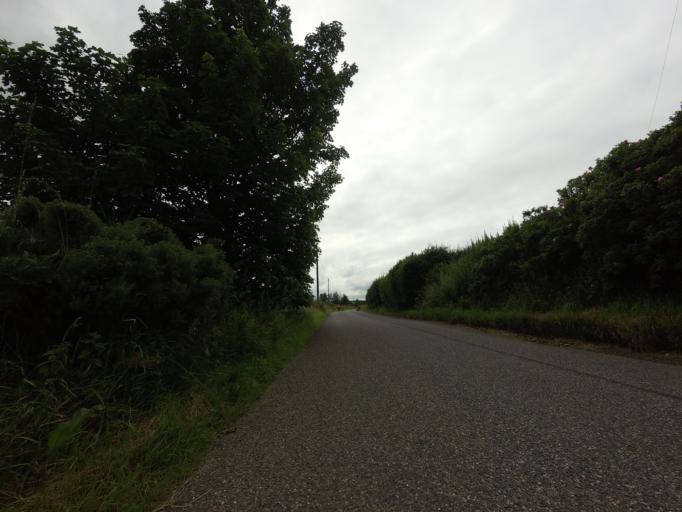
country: GB
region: Scotland
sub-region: Aberdeenshire
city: Turriff
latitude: 57.5333
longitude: -2.3803
